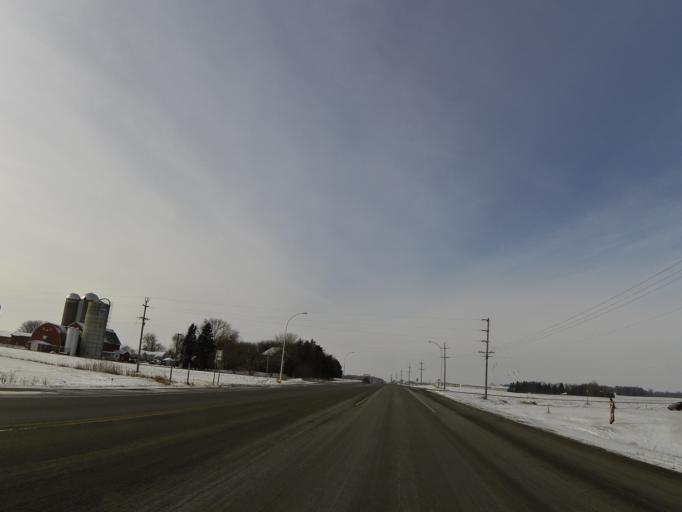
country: US
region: Minnesota
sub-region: McLeod County
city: Lester Prairie
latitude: 44.9064
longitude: -94.0313
